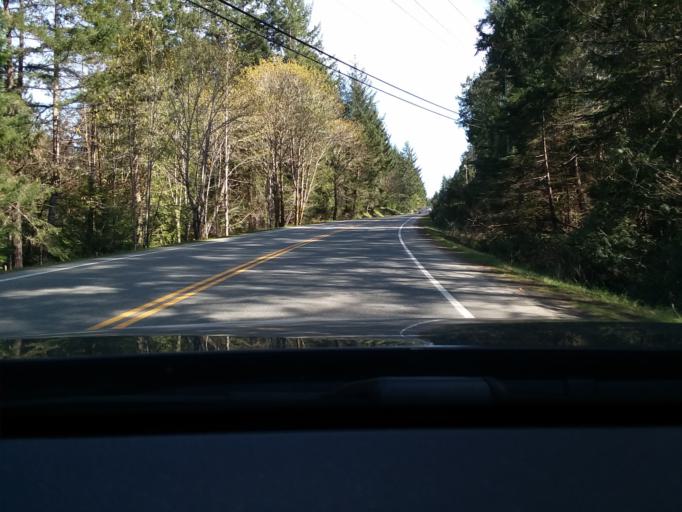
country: CA
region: British Columbia
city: North Saanich
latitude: 48.8535
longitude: -123.4658
